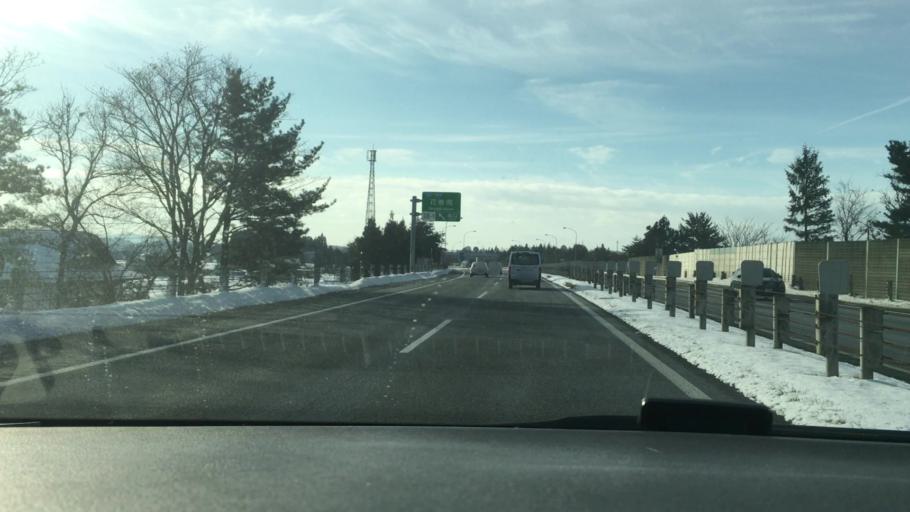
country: JP
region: Iwate
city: Hanamaki
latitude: 39.3906
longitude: 141.0917
